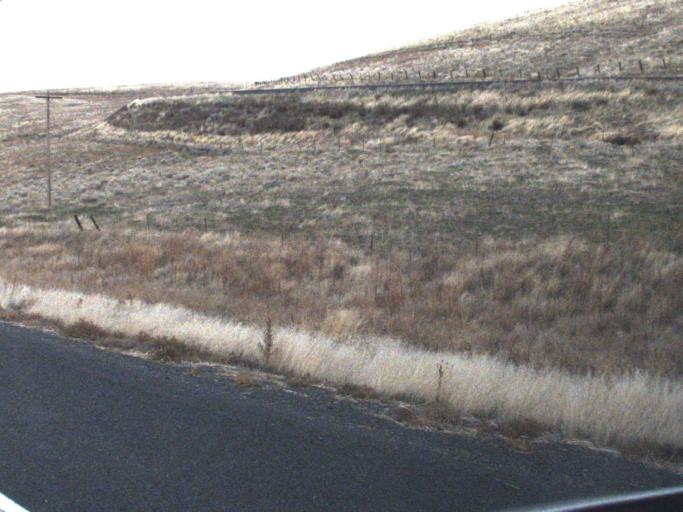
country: US
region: Washington
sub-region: Adams County
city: Ritzville
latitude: 46.7790
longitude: -118.0848
